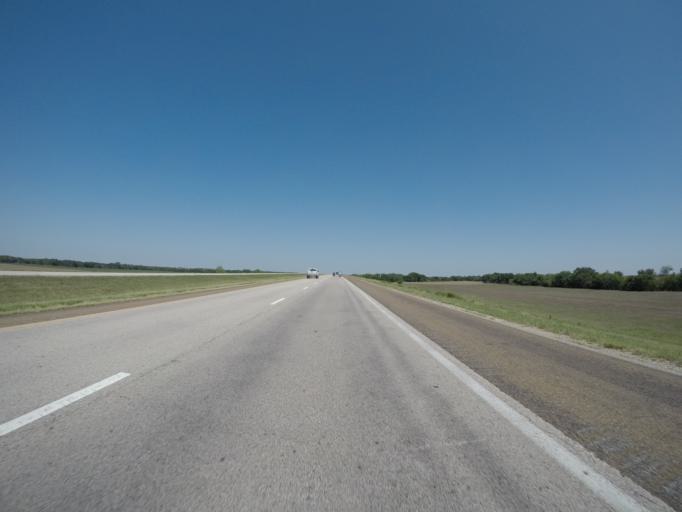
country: US
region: Kansas
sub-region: Saline County
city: Salina
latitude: 38.8780
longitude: -97.8116
